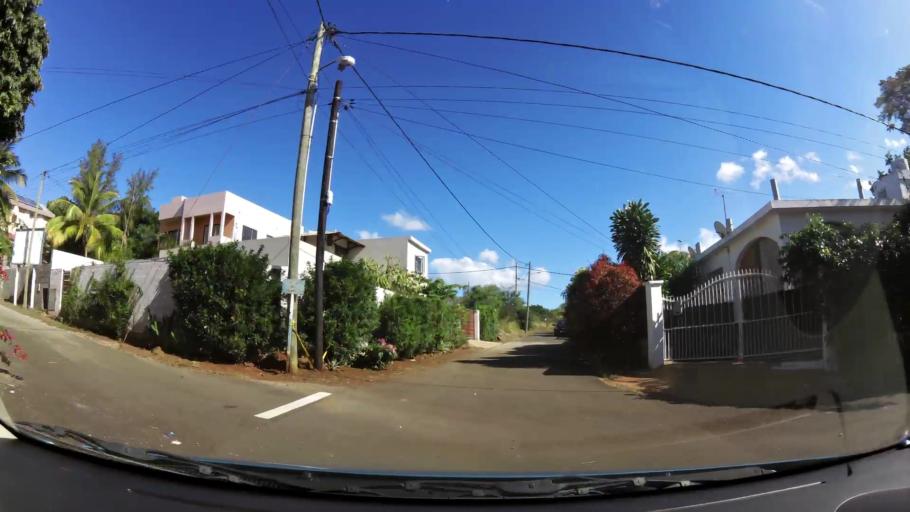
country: MU
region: Black River
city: Albion
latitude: -20.2193
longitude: 57.4029
